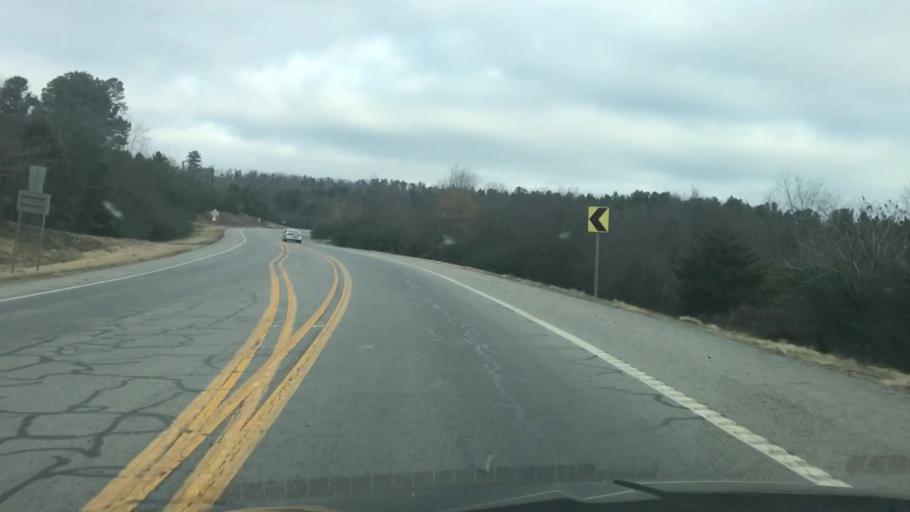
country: US
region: Arkansas
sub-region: Scott County
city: Waldron
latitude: 34.8094
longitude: -94.0395
